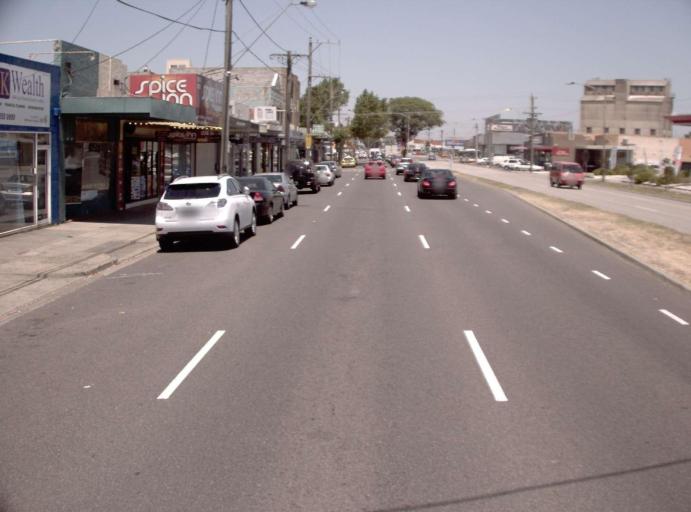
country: AU
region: Victoria
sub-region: Greater Dandenong
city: Springvale
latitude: -37.9462
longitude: 145.1534
